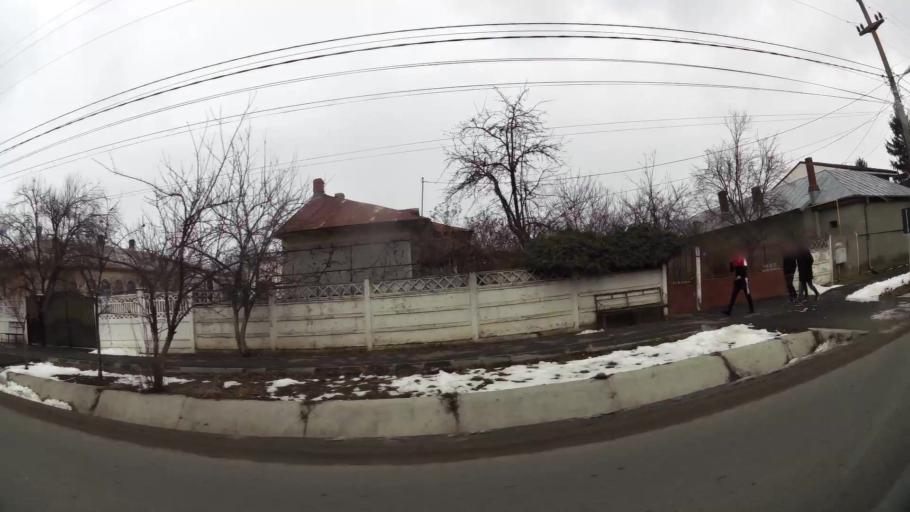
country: RO
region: Ilfov
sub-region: Comuna Afumati
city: Afumati
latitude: 44.5252
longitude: 26.2468
